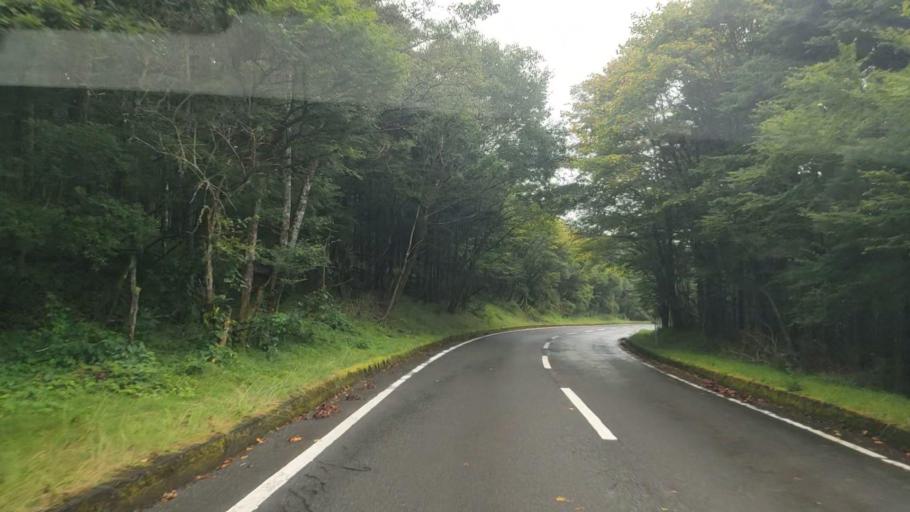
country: JP
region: Shizuoka
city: Fuji
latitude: 35.3055
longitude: 138.7443
